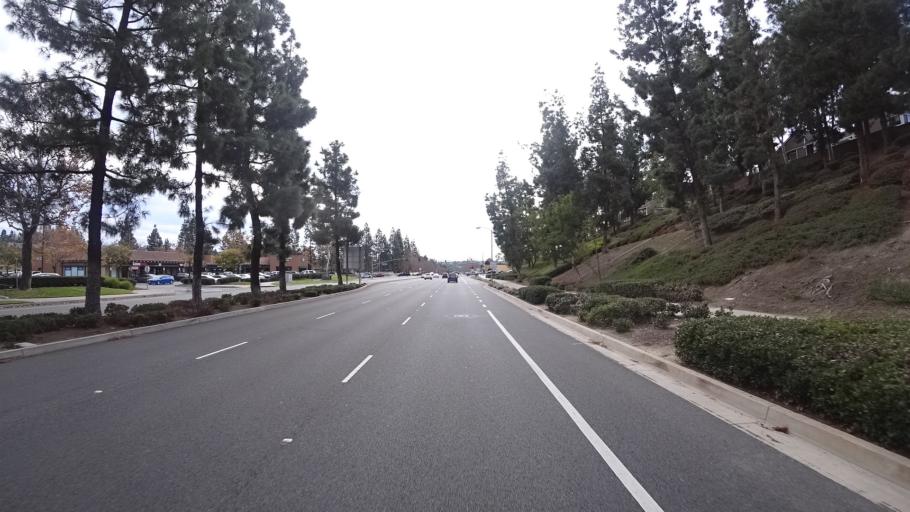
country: US
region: California
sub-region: Orange County
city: Aliso Viejo
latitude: 33.5709
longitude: -117.7077
